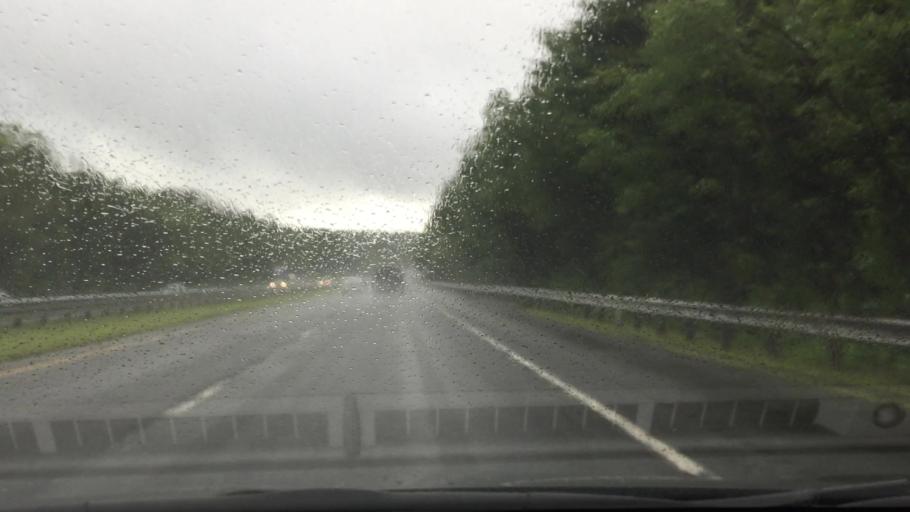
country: US
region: Massachusetts
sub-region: Worcester County
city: Warren
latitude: 42.1695
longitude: -72.1851
